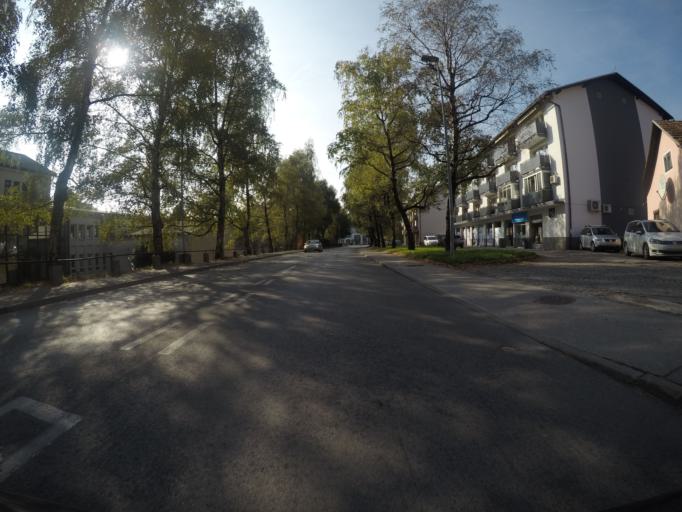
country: SI
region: Kamnik
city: Kamnik
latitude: 46.2210
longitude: 14.6060
